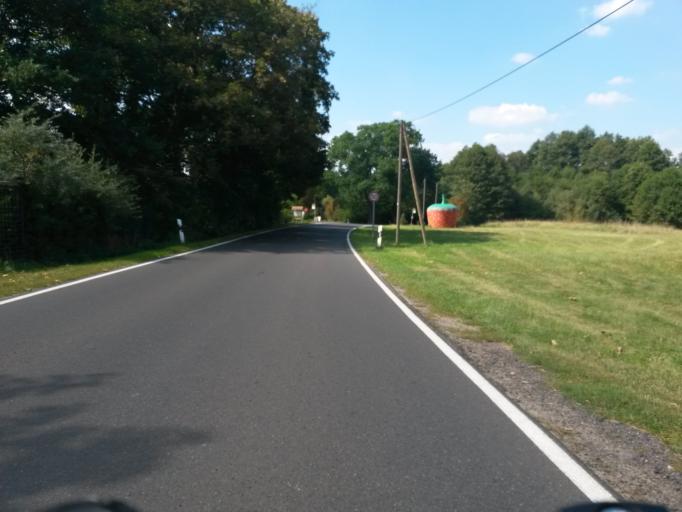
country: DE
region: Brandenburg
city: Milmersdorf
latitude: 53.0542
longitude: 13.5730
